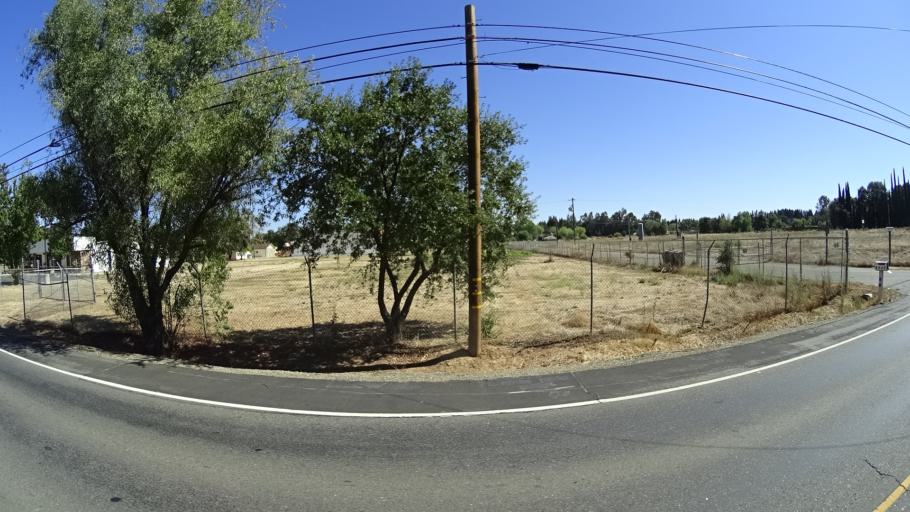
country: US
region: California
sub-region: Sacramento County
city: Vineyard
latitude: 38.4330
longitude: -121.3347
